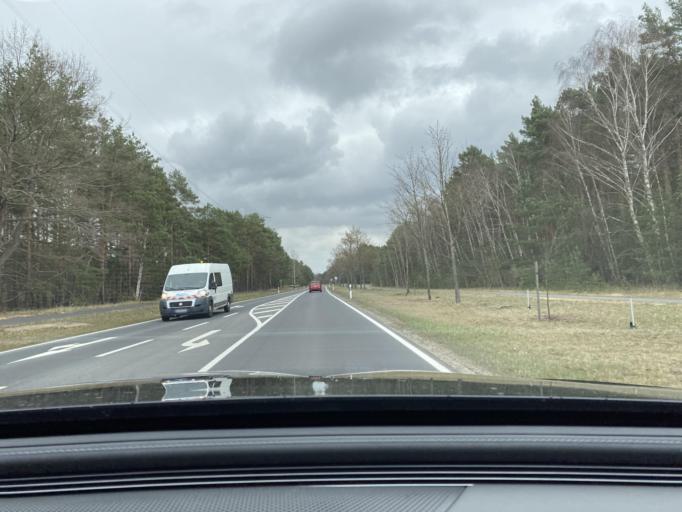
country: DE
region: Saxony
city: Boxberg
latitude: 51.4095
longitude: 14.5621
